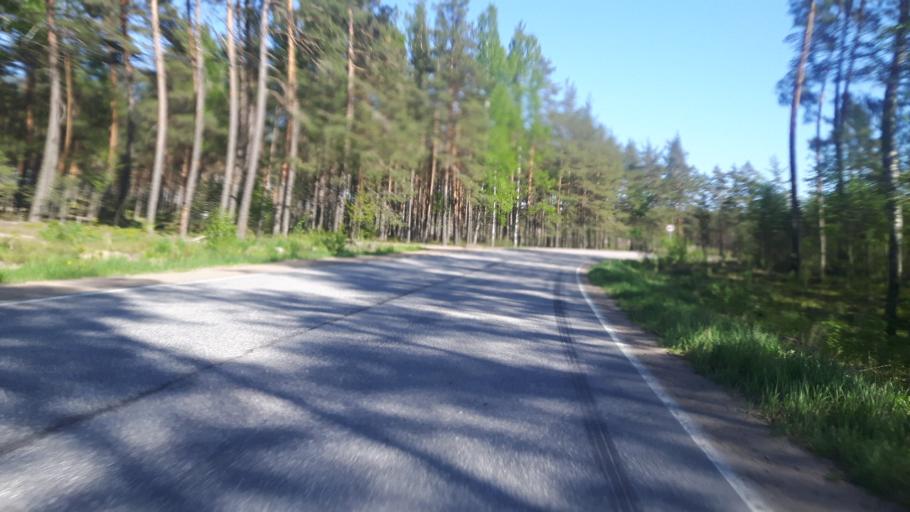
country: RU
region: Leningrad
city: Glebychevo
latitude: 60.2775
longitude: 28.9205
